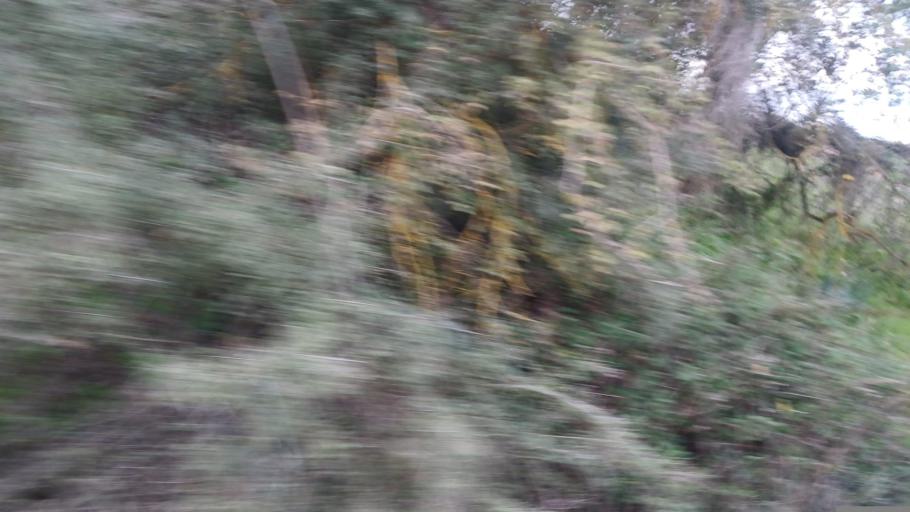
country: CY
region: Pafos
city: Mesogi
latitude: 34.8696
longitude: 32.5147
